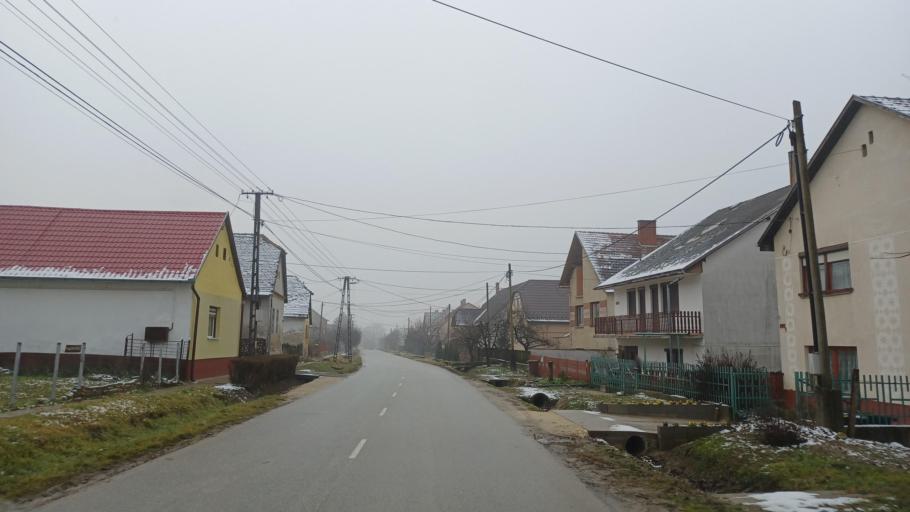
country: HU
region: Tolna
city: Gyonk
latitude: 46.5664
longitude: 18.4757
